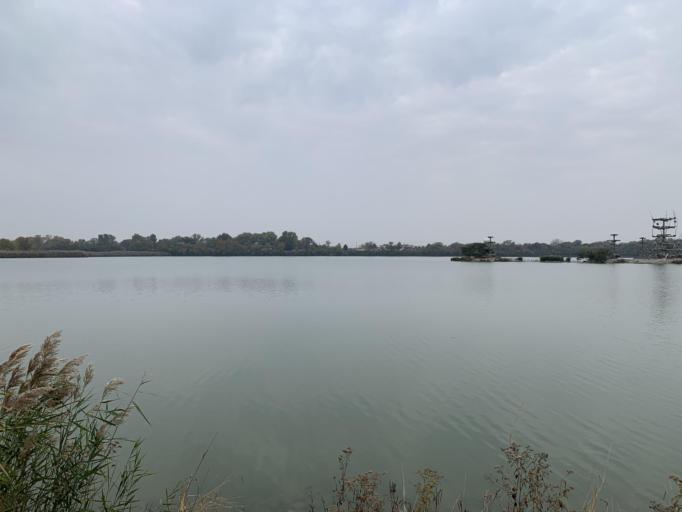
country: US
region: Illinois
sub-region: Will County
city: Plainfield
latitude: 41.6003
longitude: -88.1859
